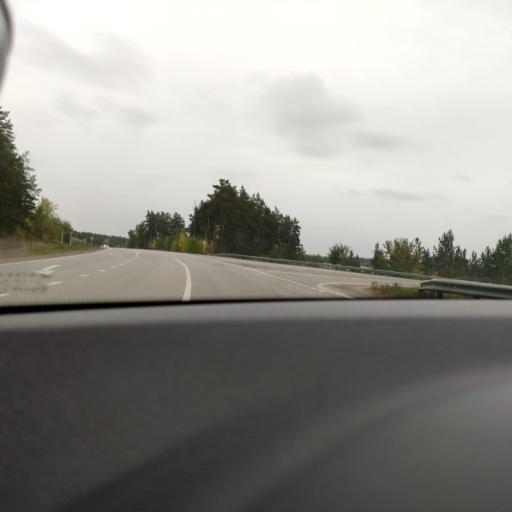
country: RU
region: Samara
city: Mirnyy
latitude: 53.5417
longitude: 50.2970
